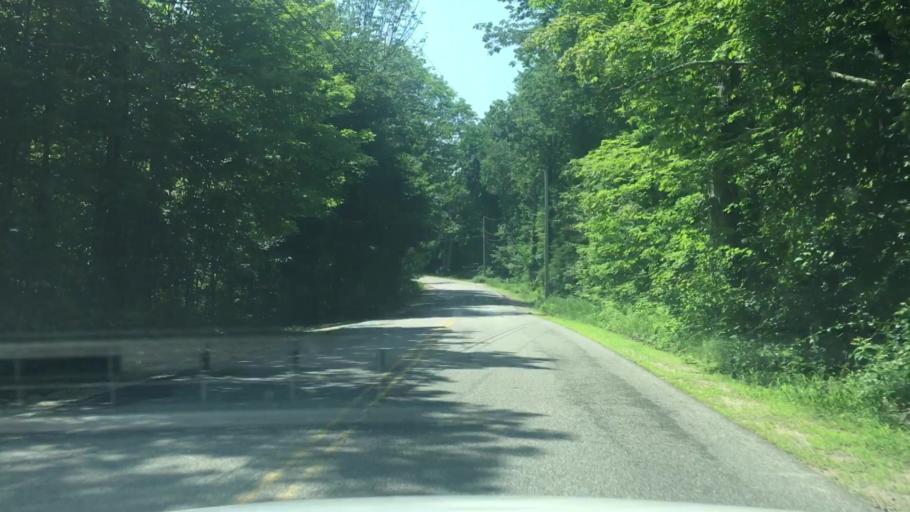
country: US
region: Maine
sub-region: Cumberland County
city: Cumberland Center
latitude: 43.8417
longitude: -70.3103
